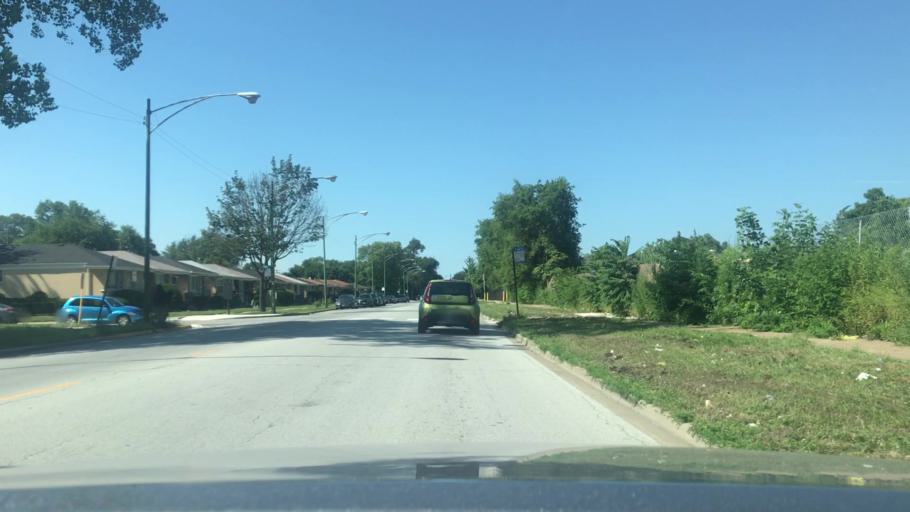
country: US
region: Illinois
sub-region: Cook County
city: Burnham
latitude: 41.7096
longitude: -87.5596
